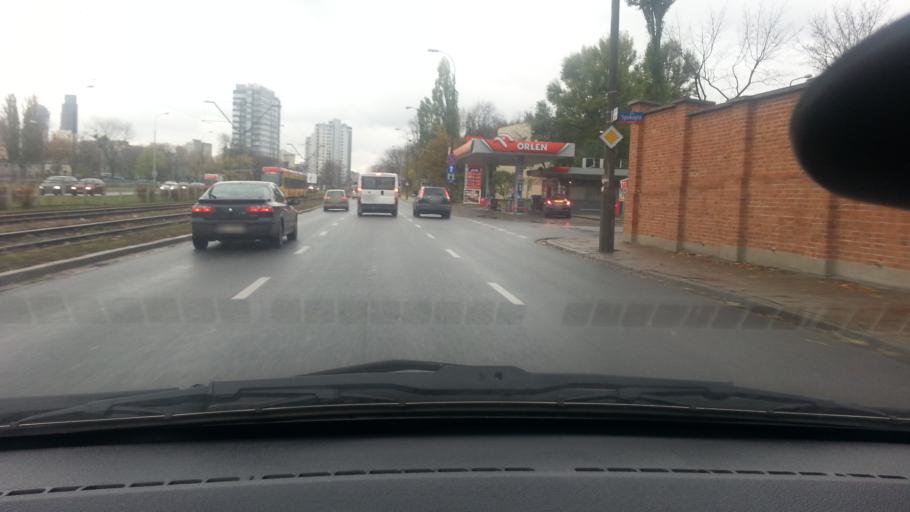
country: PL
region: Masovian Voivodeship
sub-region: Warszawa
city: Wola
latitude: 52.2520
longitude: 20.9805
